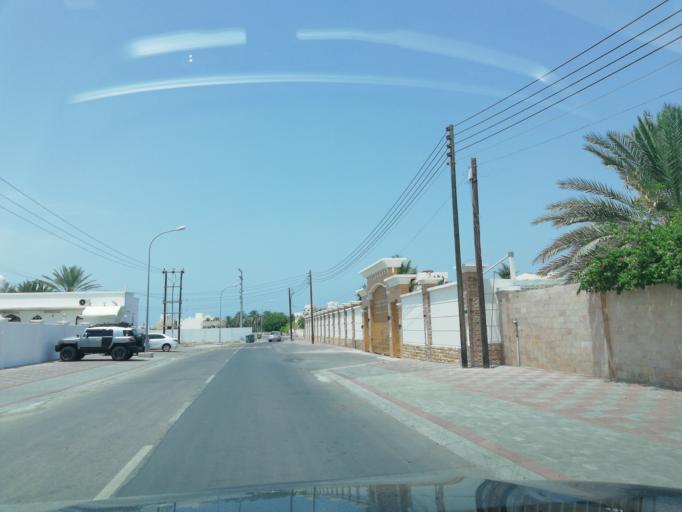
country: OM
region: Muhafazat Masqat
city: As Sib al Jadidah
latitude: 23.6600
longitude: 58.1949
